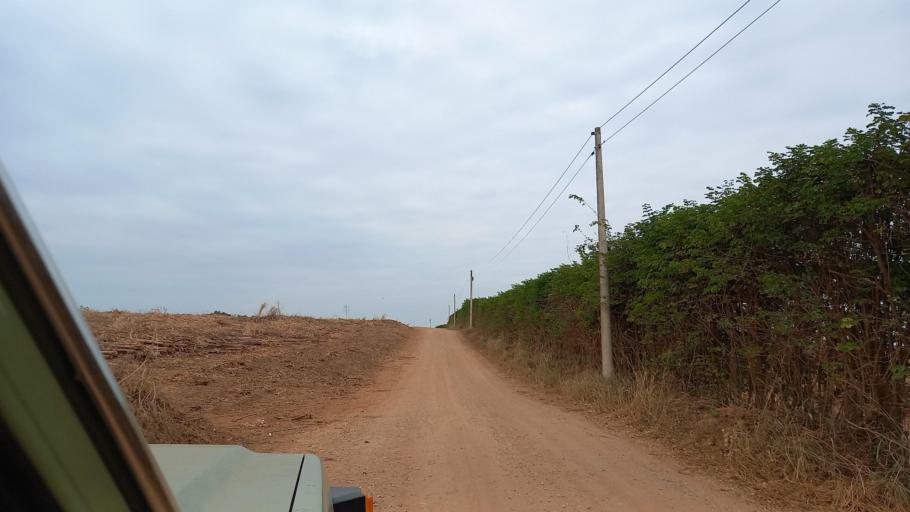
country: BR
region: Sao Paulo
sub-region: Moji-Guacu
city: Mogi-Gaucu
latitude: -22.2780
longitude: -46.8450
